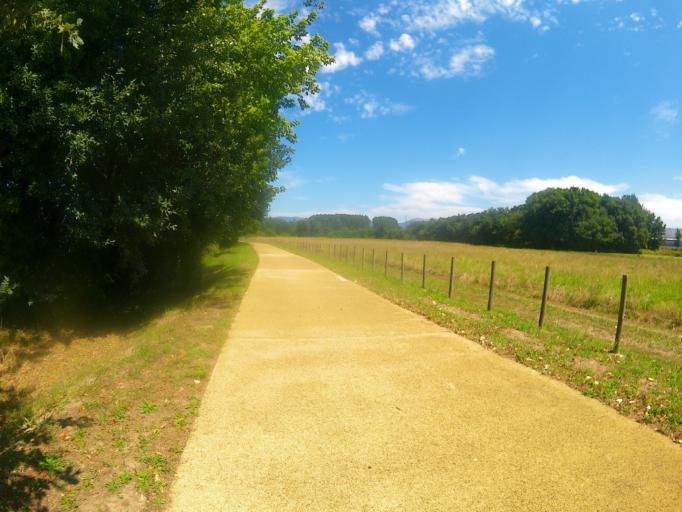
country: ES
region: Galicia
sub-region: Provincia de Pontevedra
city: Tomino
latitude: 41.9826
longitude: -8.6972
